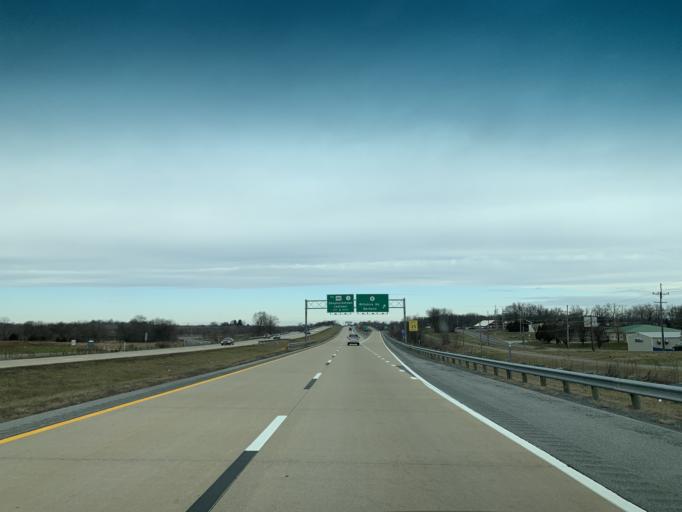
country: US
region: West Virginia
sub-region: Jefferson County
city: Ranson
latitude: 39.3584
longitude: -77.8614
